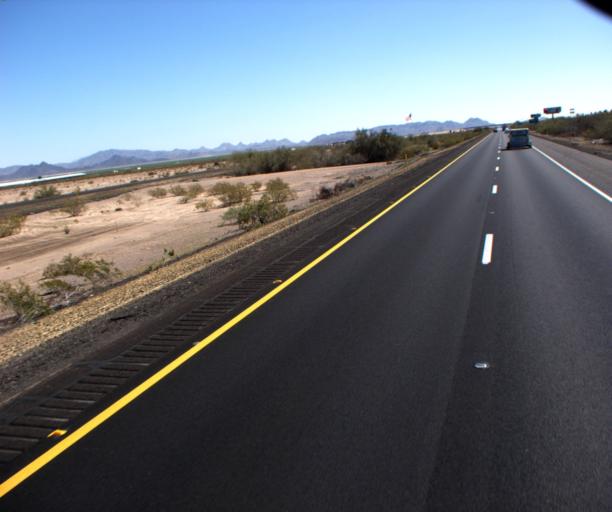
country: US
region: Arizona
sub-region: La Paz County
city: Salome
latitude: 33.6329
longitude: -113.7825
